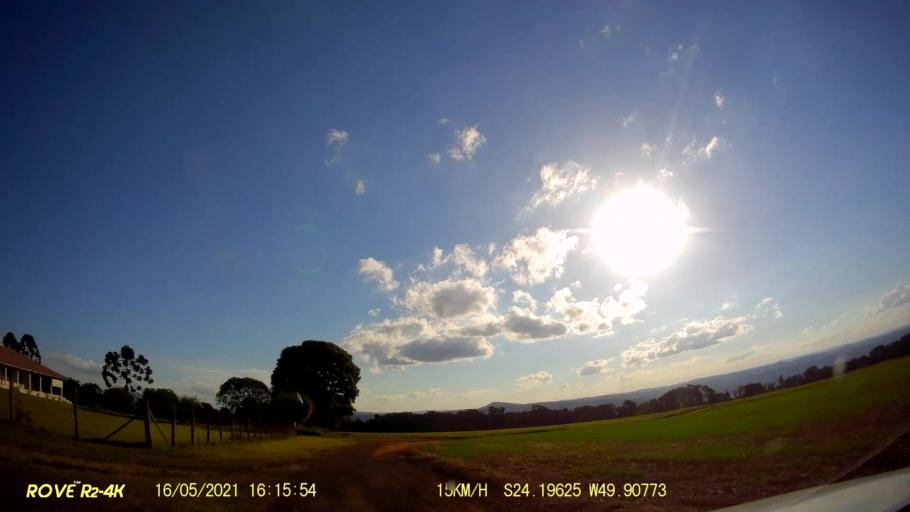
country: BR
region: Parana
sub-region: Jaguariaiva
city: Jaguariaiva
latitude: -24.1962
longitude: -49.9078
